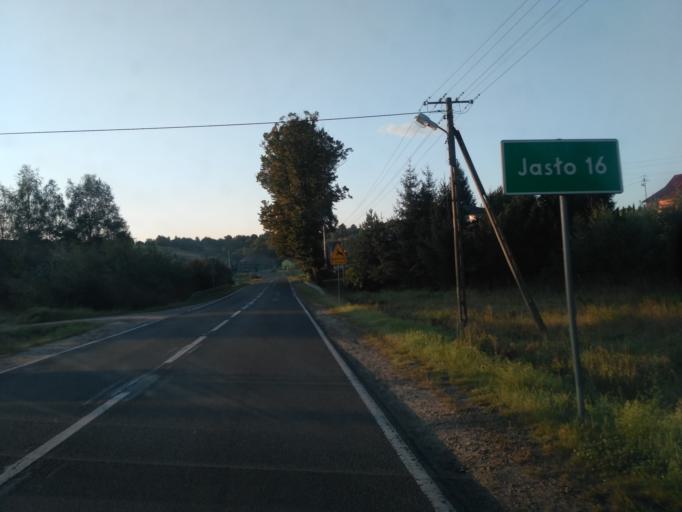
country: PL
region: Subcarpathian Voivodeship
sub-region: Powiat strzyzowski
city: Frysztak
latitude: 49.8204
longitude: 21.6240
